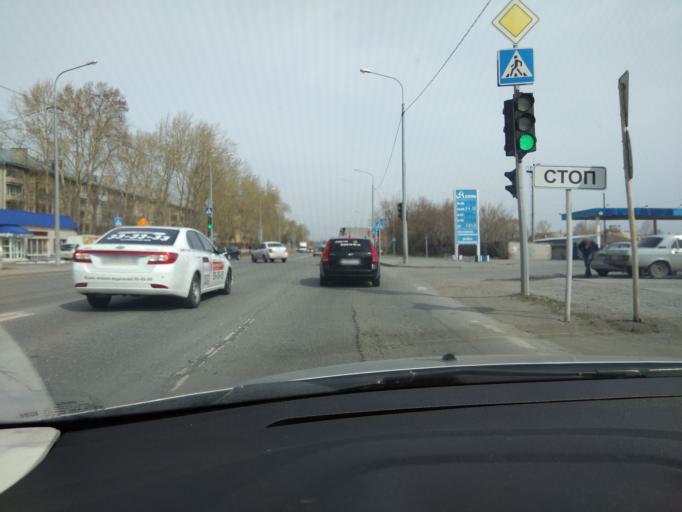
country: RU
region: Tjumen
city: Melioratorov
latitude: 57.1831
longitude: 65.5922
